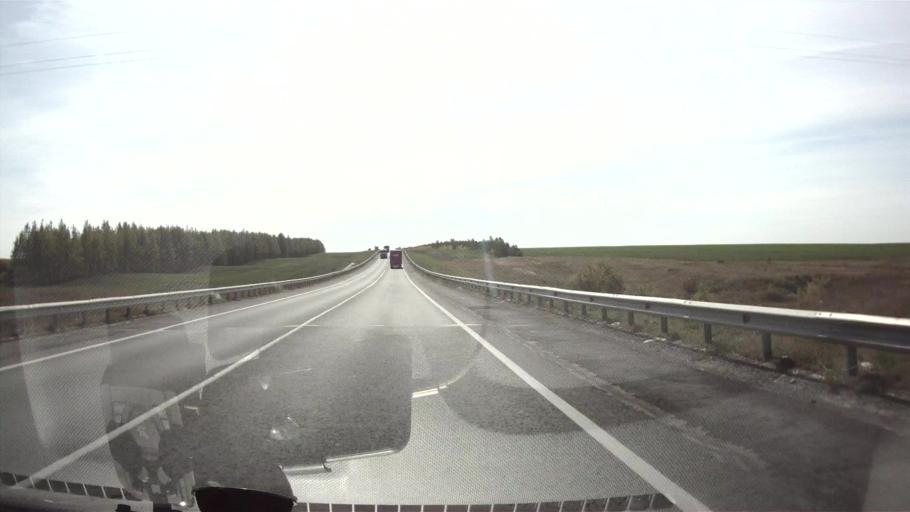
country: RU
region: Samara
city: Syzran'
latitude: 52.9012
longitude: 48.2966
